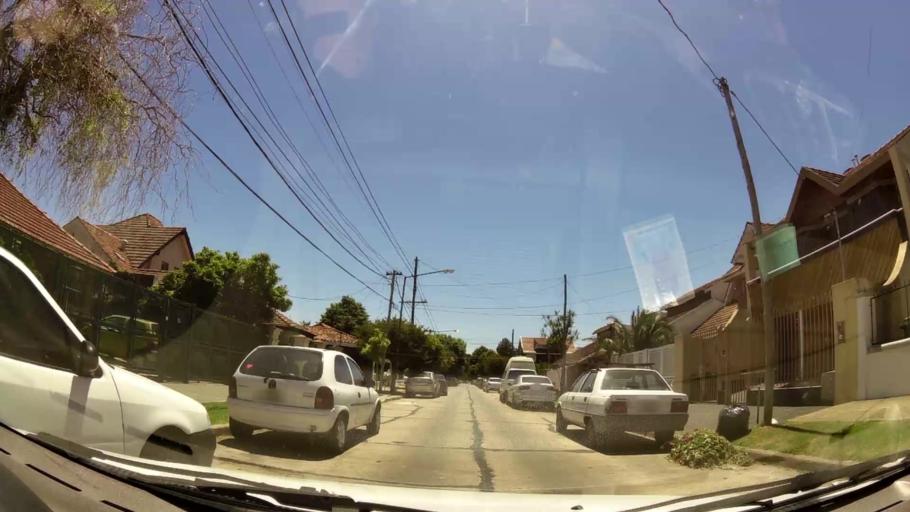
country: AR
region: Buenos Aires
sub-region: Partido de San Isidro
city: San Isidro
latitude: -34.4893
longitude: -58.5208
